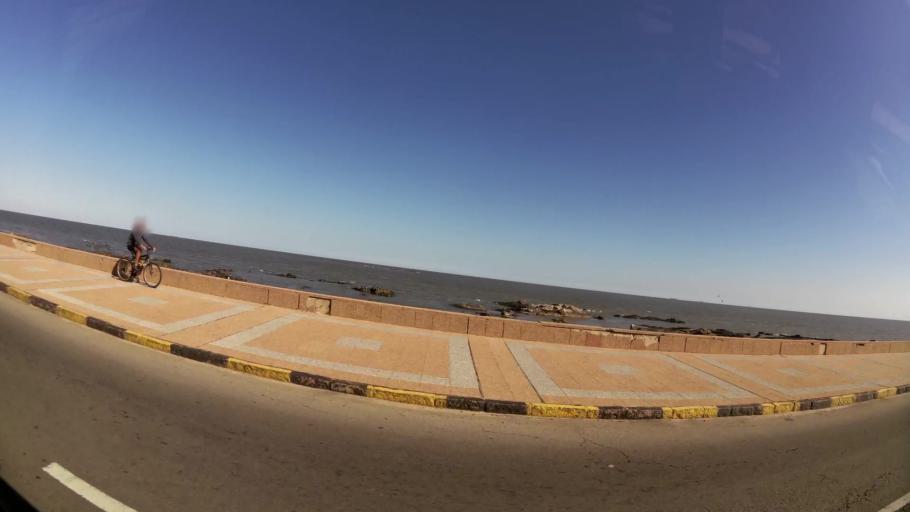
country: UY
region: Canelones
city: Paso de Carrasco
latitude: -34.8990
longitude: -56.0644
